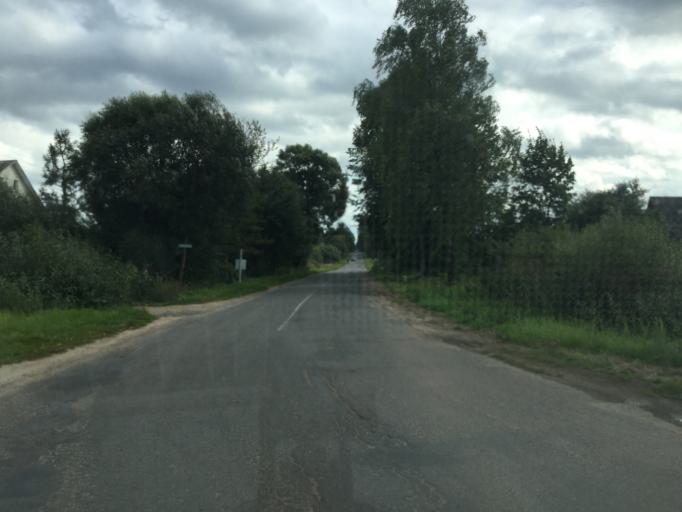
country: BY
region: Vitebsk
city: Vitebsk
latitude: 55.1485
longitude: 30.2791
